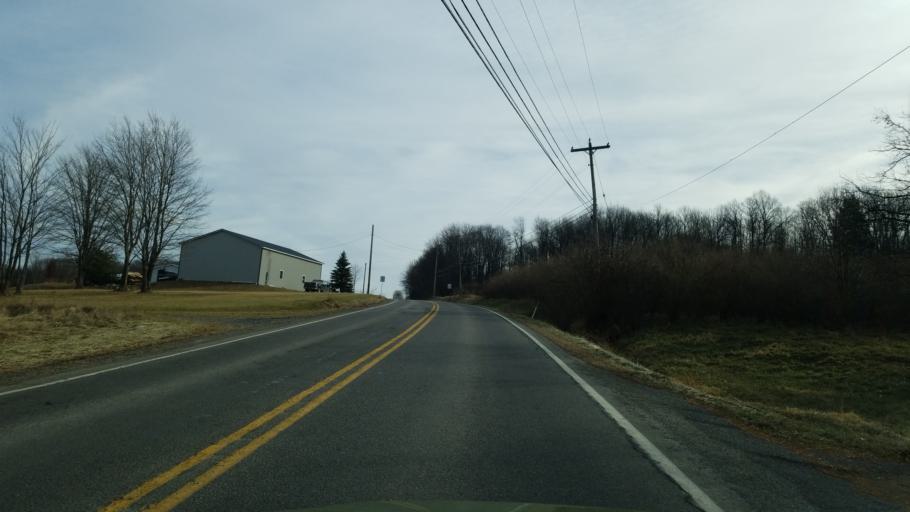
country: US
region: Pennsylvania
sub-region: Indiana County
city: Johnsonburg
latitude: 40.9217
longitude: -78.8617
